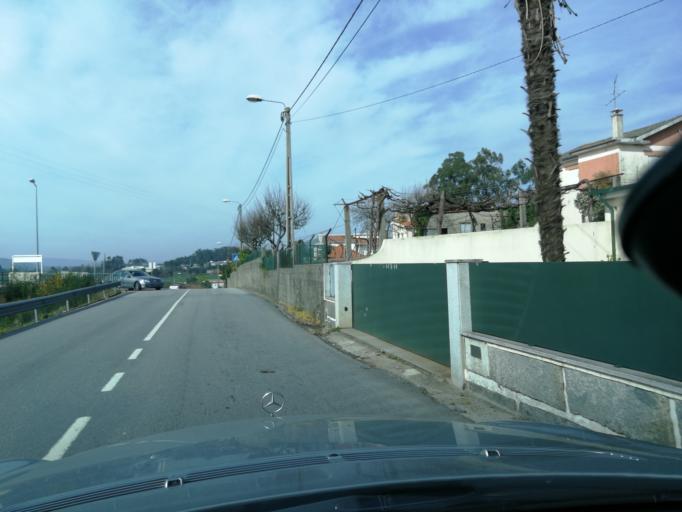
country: PT
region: Braga
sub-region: Vila Nova de Famalicao
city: Vila Nova de Famalicao
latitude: 41.4291
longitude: -8.5218
